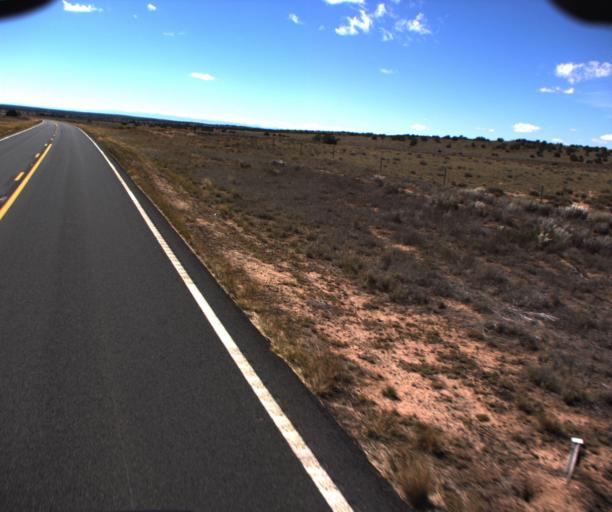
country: US
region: Arizona
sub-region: Apache County
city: Houck
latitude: 34.9326
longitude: -109.2371
